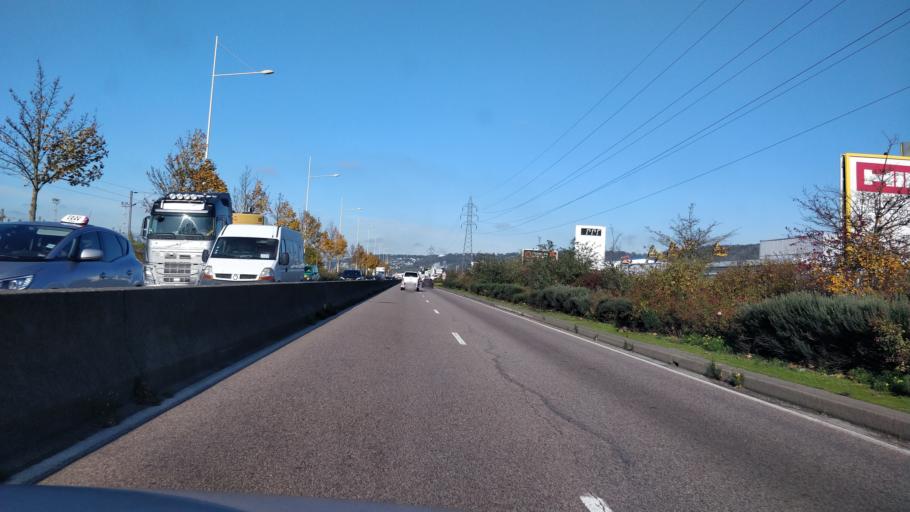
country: FR
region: Haute-Normandie
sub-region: Departement de la Seine-Maritime
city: Saint-Etienne-du-Rouvray
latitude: 49.3908
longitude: 1.1111
